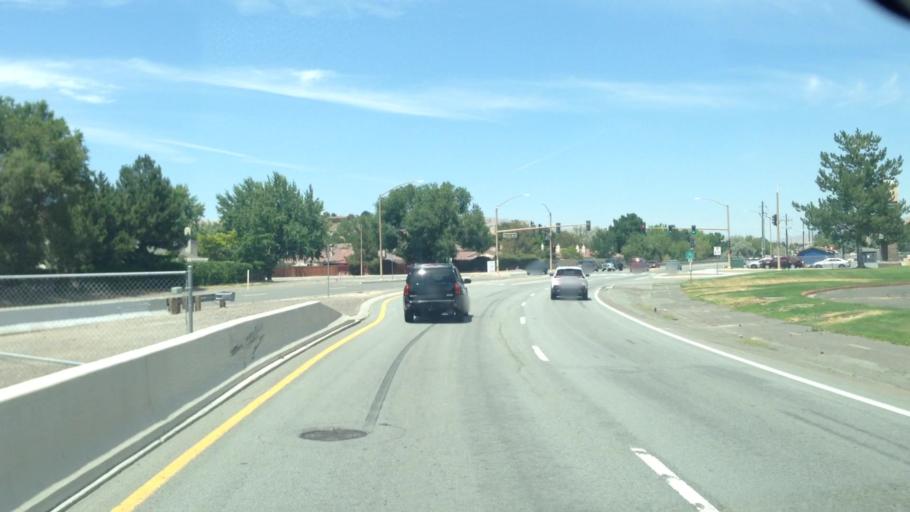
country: US
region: Nevada
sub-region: Washoe County
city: Sparks
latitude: 39.5552
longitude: -119.7241
